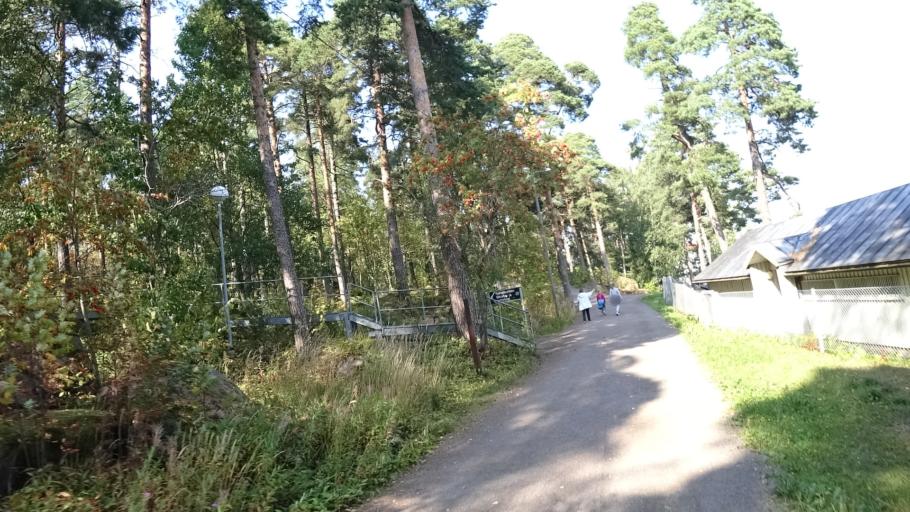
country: FI
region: Kymenlaakso
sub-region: Kotka-Hamina
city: Kotka
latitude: 60.4544
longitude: 26.9514
